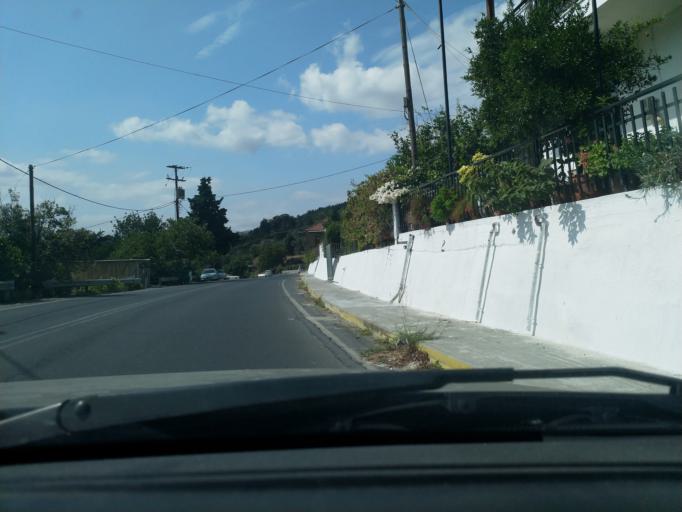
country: GR
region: Crete
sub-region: Nomos Rethymnis
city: Agia Foteini
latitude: 35.2198
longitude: 24.5210
